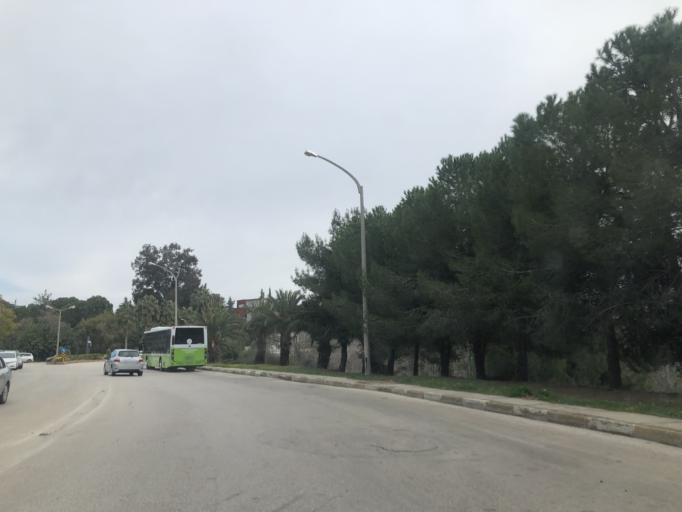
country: TR
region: Adana
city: Adana
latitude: 37.0565
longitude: 35.3558
